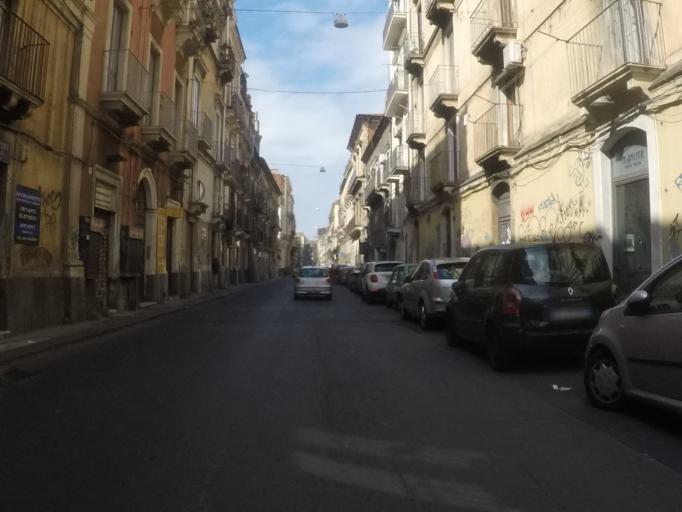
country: IT
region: Sicily
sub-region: Catania
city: Catania
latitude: 37.5052
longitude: 15.0922
